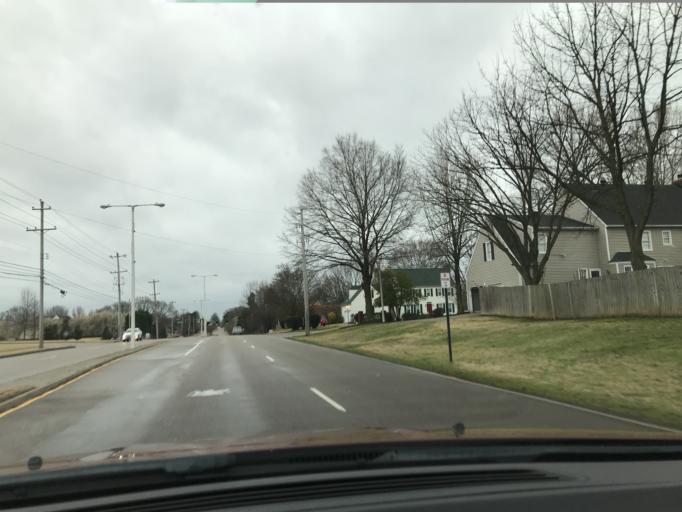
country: US
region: Tennessee
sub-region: Shelby County
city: Collierville
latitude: 35.0633
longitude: -89.6859
